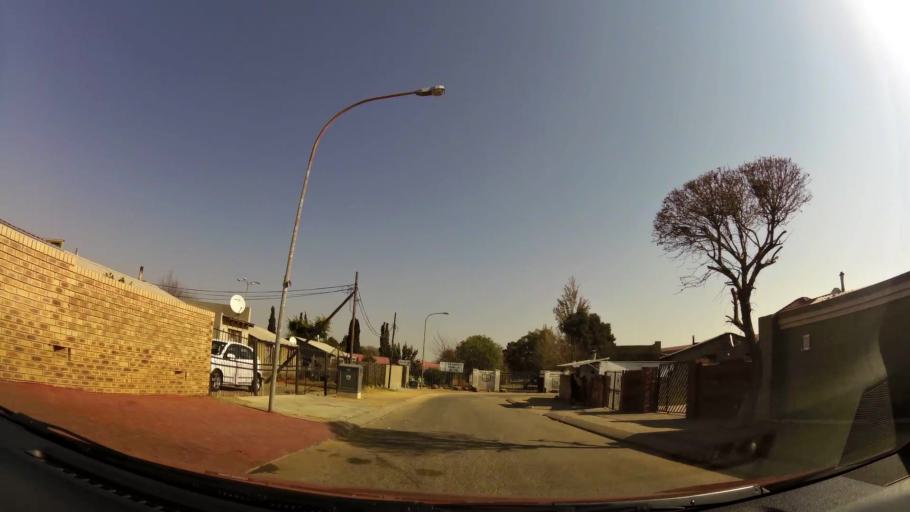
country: ZA
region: Gauteng
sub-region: City of Johannesburg Metropolitan Municipality
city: Soweto
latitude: -26.2465
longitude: 27.9533
